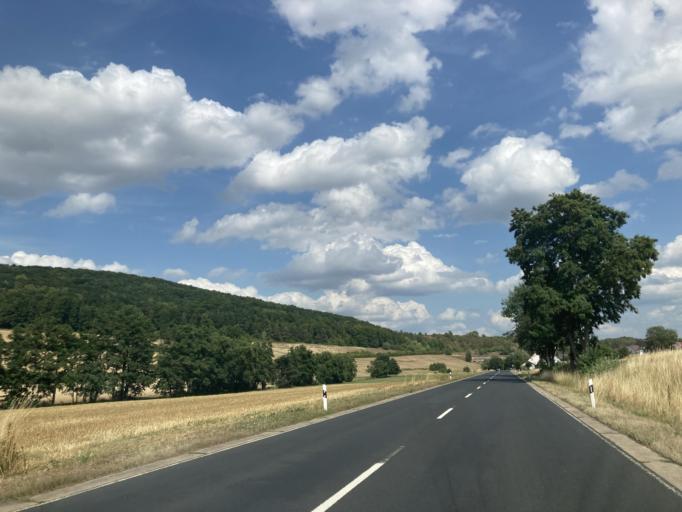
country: DE
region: Hesse
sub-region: Regierungsbezirk Kassel
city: Grossenluder
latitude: 50.5410
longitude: 9.5957
